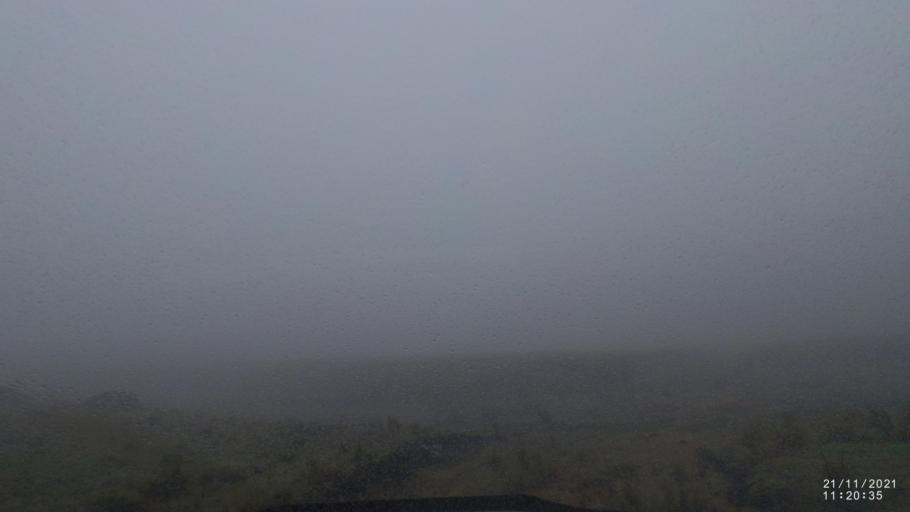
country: BO
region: Cochabamba
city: Cochabamba
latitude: -16.9610
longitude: -66.2694
